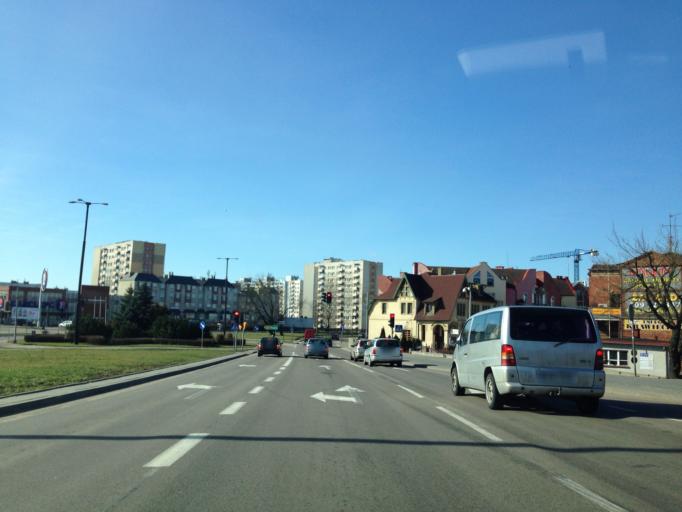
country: PL
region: Pomeranian Voivodeship
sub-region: Powiat malborski
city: Malbork
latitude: 54.0368
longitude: 19.0383
